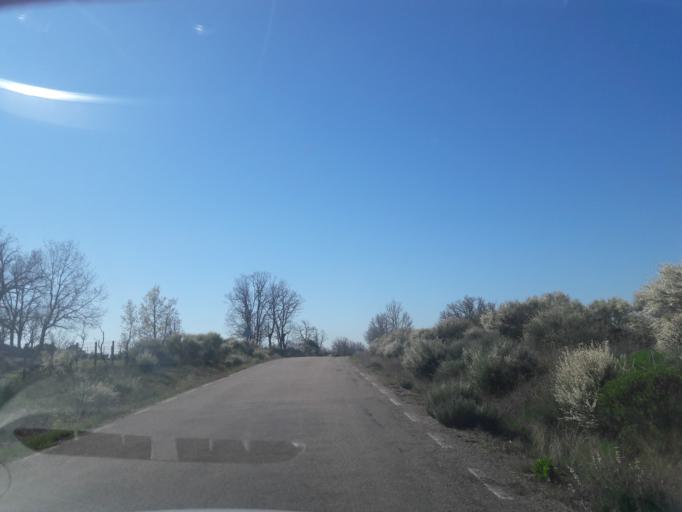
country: ES
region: Castille and Leon
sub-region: Provincia de Salamanca
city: Valsalabroso
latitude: 41.1250
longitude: -6.4819
